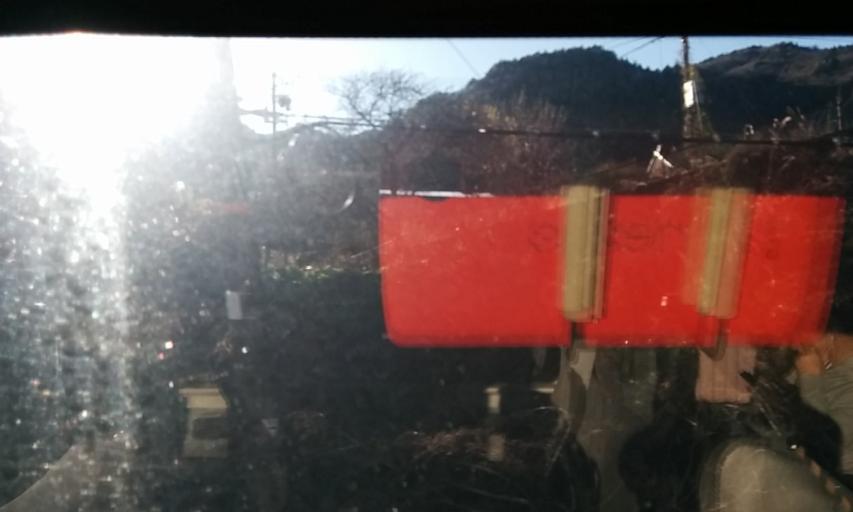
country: JP
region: Nagano
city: Ina
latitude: 35.8125
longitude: 137.6839
